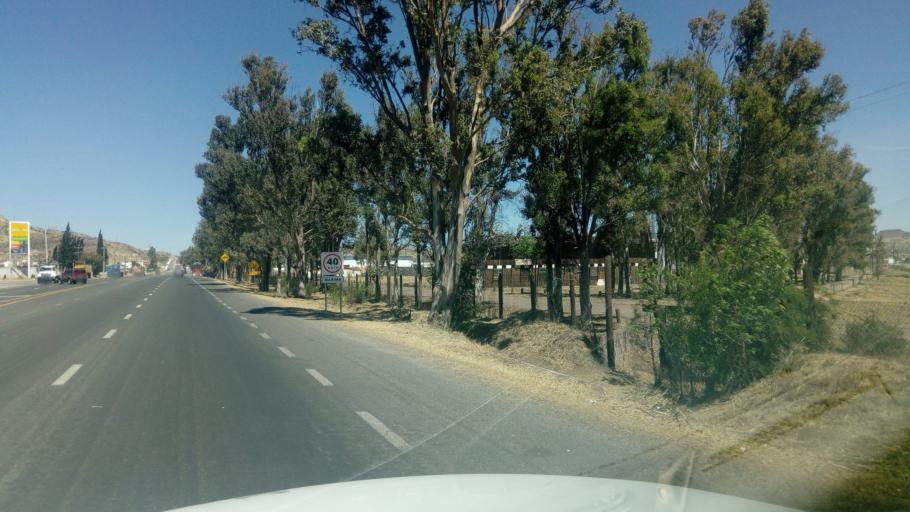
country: MX
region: Durango
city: Victoria de Durango
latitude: 24.0761
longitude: -104.6634
